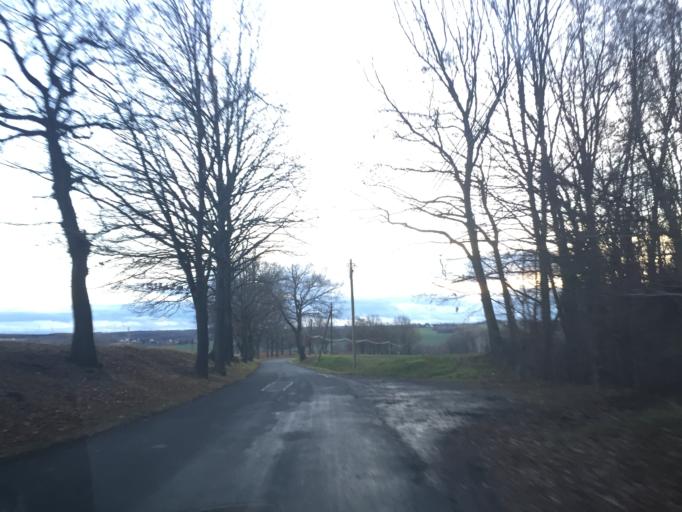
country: DE
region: Thuringia
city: Schmolln
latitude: 50.8984
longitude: 12.3322
